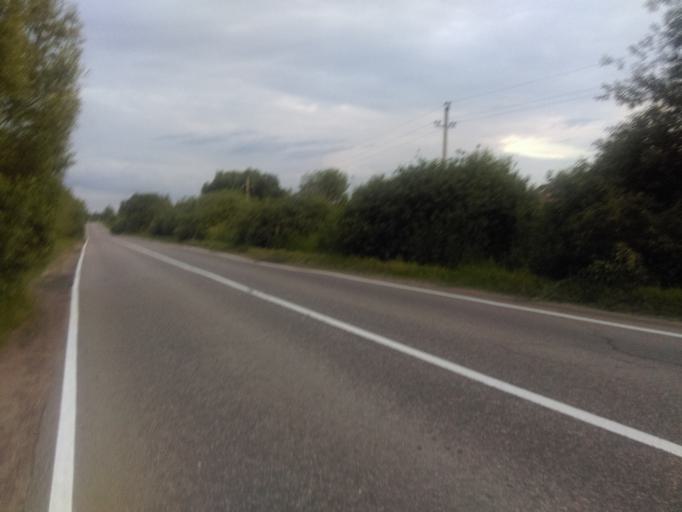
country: RU
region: Moskovskaya
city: Vostryakovo
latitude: 55.3899
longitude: 37.8081
